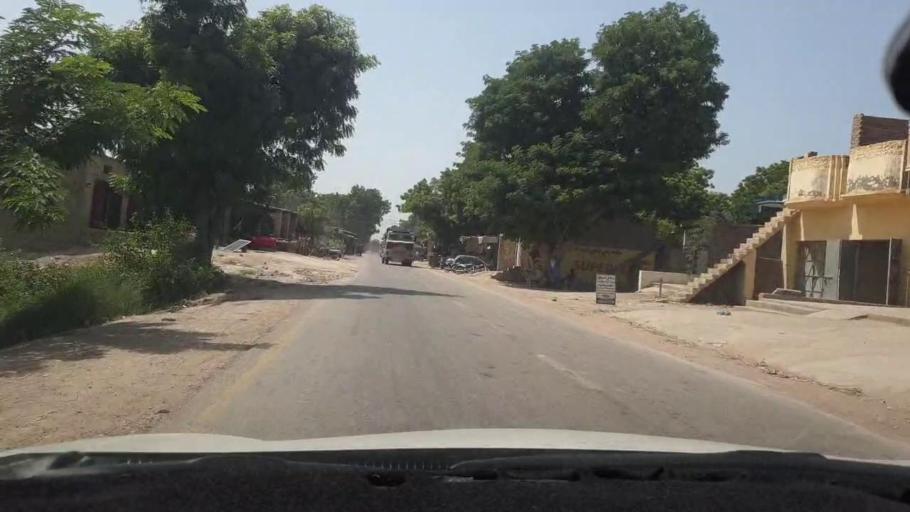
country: PK
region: Sindh
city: Bhit Shah
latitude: 25.8532
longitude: 68.4936
